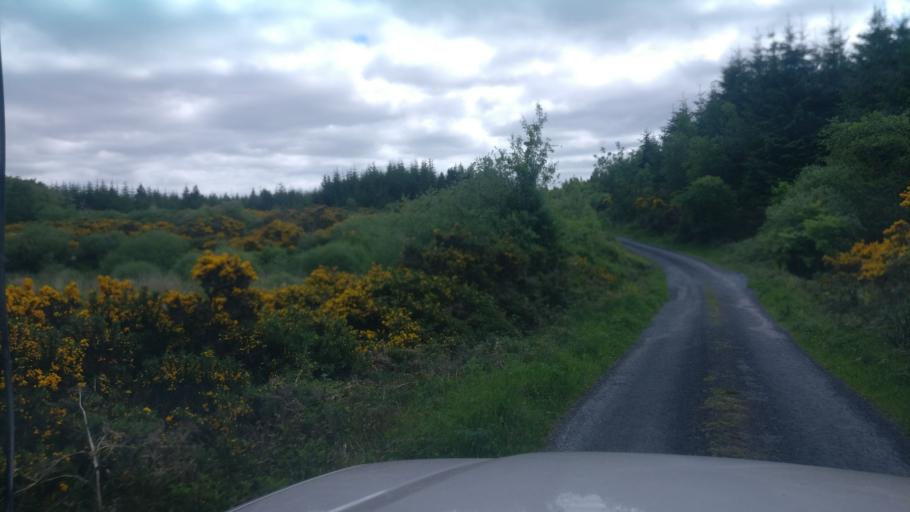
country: IE
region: Connaught
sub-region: County Galway
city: Gort
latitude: 53.1188
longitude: -8.6874
